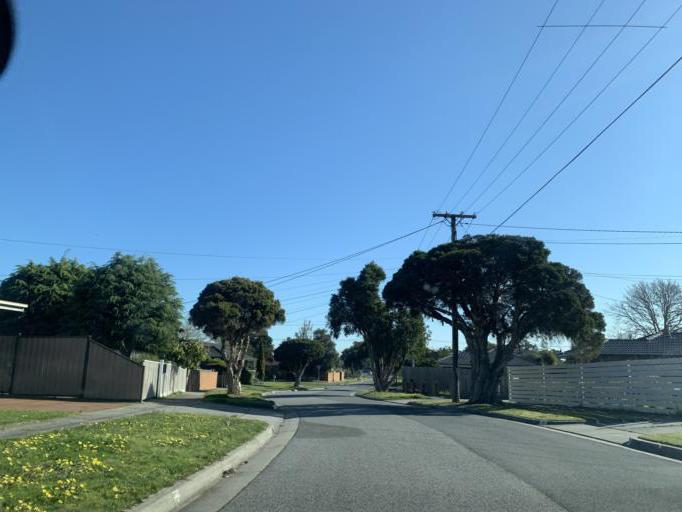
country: AU
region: Victoria
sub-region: Greater Dandenong
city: Keysborough
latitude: -37.9883
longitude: 145.1842
